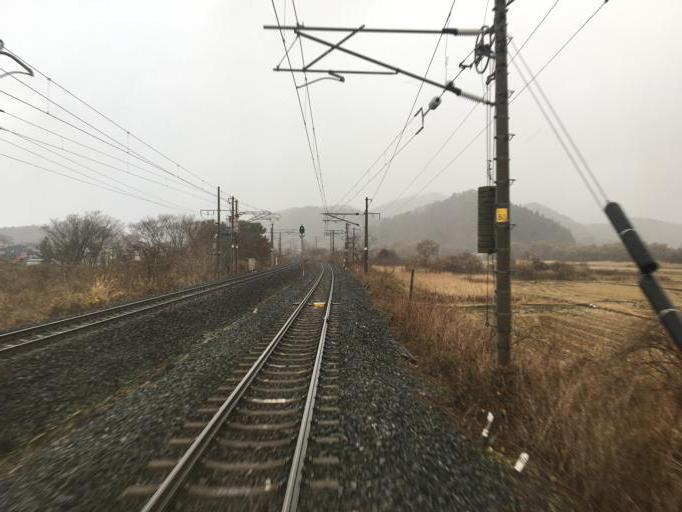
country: JP
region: Aomori
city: Aomori Shi
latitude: 40.8475
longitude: 140.8184
